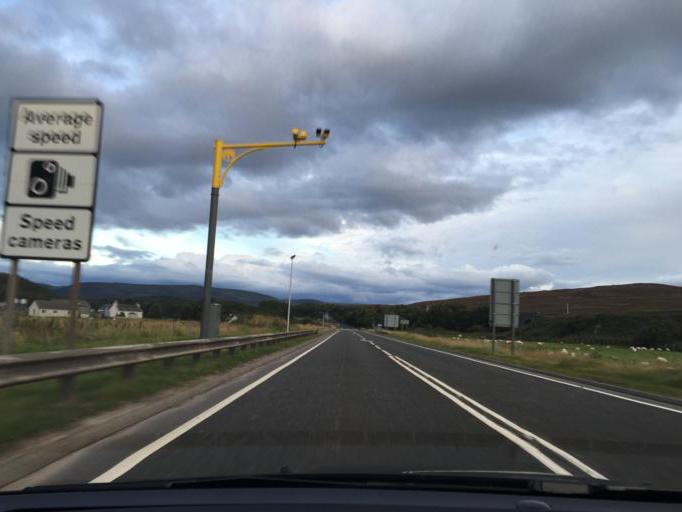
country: GB
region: Scotland
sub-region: Highland
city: Inverness
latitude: 57.3661
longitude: -4.0217
